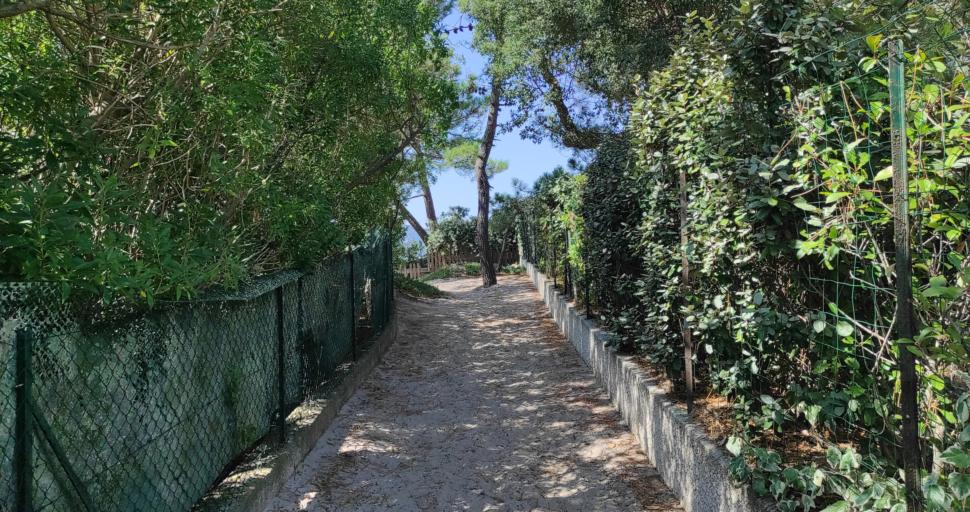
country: FR
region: Corsica
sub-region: Departement de la Corse-du-Sud
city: Porto-Vecchio
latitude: 41.6221
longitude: 9.3358
